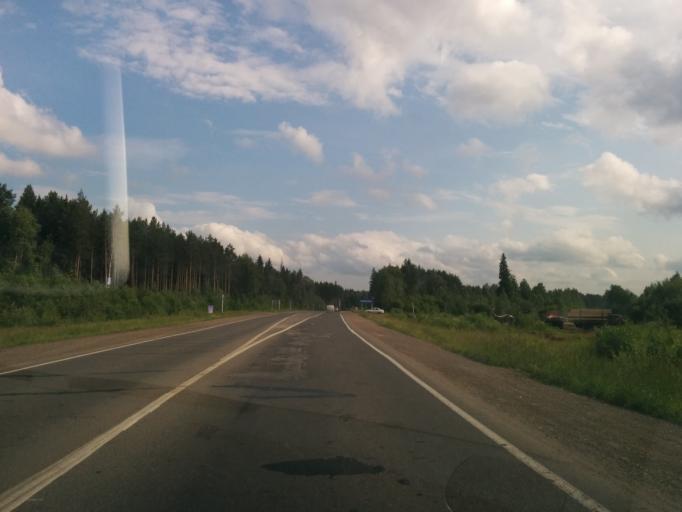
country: RU
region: Perm
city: Polazna
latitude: 58.1152
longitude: 56.4261
